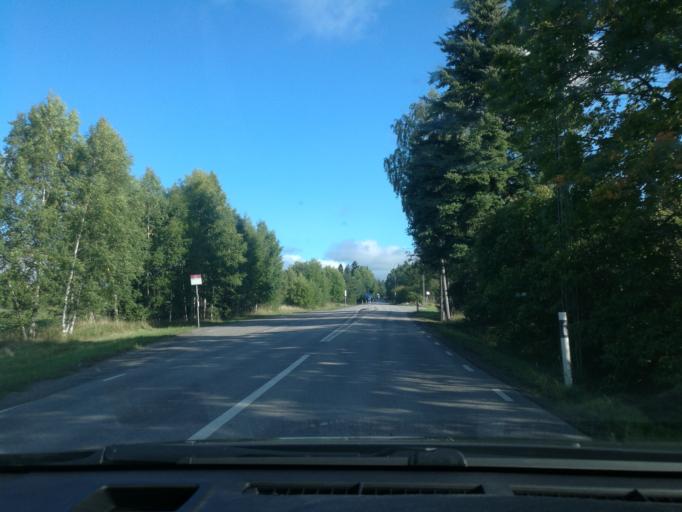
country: SE
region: Stockholm
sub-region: Upplands Vasby Kommun
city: Upplands Vaesby
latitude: 59.5263
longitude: 17.9646
